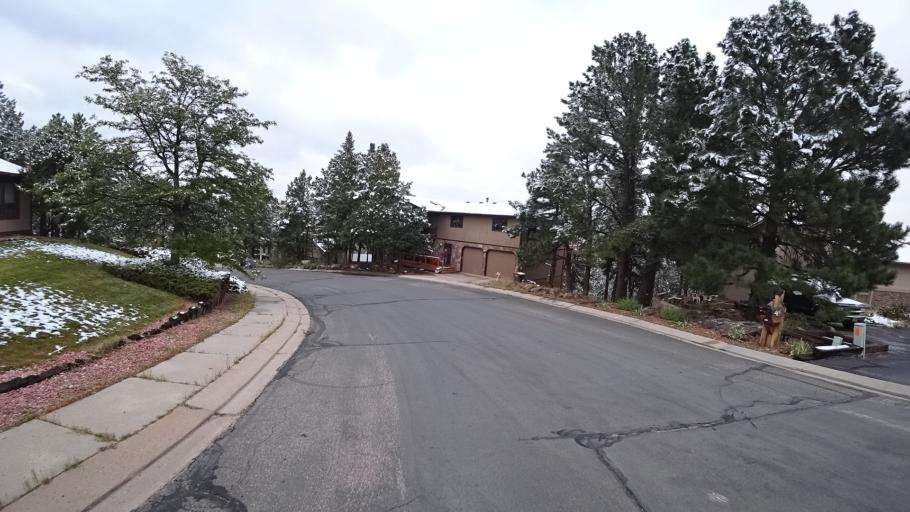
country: US
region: Colorado
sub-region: El Paso County
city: Colorado Springs
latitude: 38.9151
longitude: -104.7964
